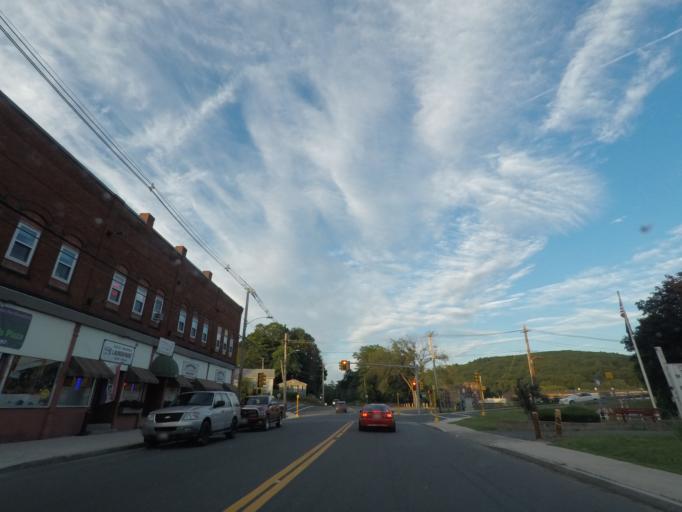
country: US
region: Massachusetts
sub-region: Worcester County
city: Warren
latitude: 42.2119
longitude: -72.2354
